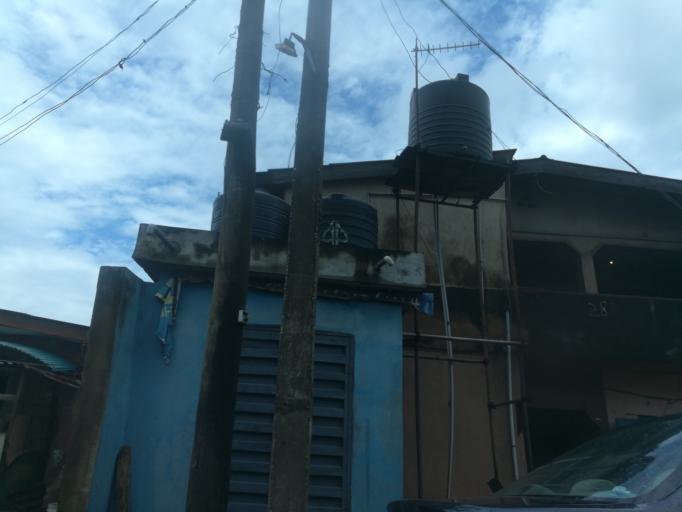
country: NG
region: Lagos
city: Agege
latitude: 6.6237
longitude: 3.3338
